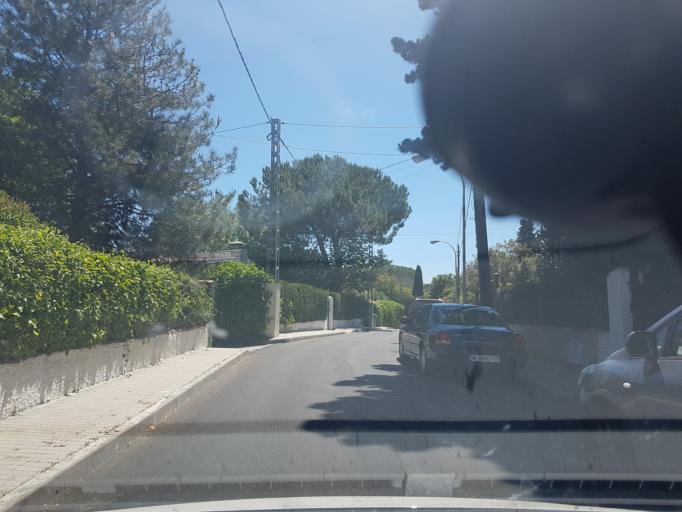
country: ES
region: Madrid
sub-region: Provincia de Madrid
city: Pozuelo de Alarcon
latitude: 40.4415
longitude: -3.8104
